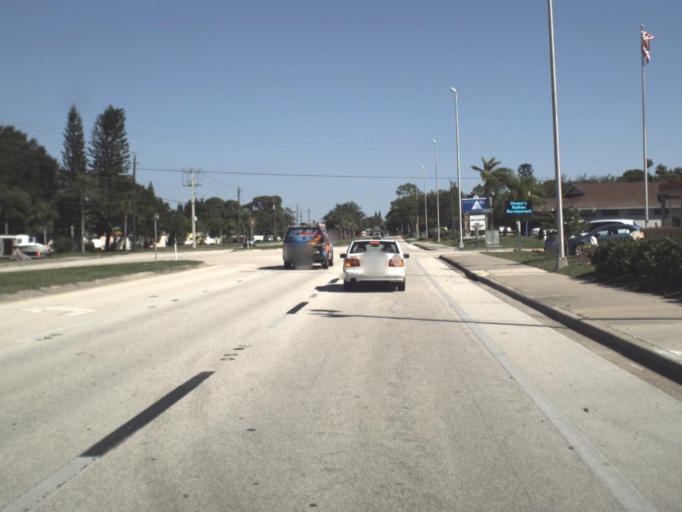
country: US
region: Florida
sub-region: Charlotte County
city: Grove City
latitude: 26.9356
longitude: -82.3295
